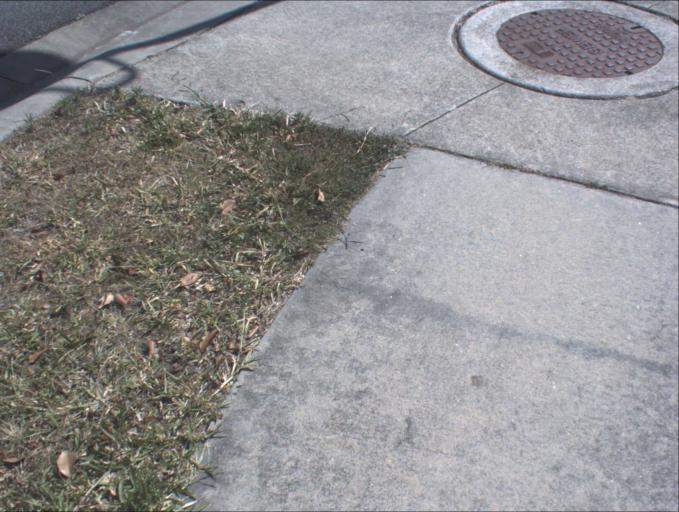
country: AU
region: Queensland
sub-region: Gold Coast
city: Yatala
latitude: -27.6930
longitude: 153.2188
